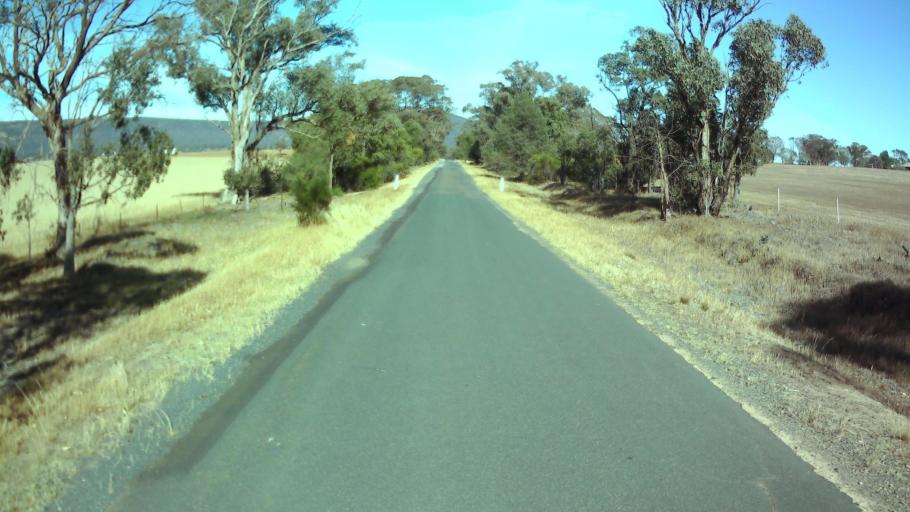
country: AU
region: New South Wales
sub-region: Weddin
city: Grenfell
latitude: -33.9054
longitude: 148.0613
